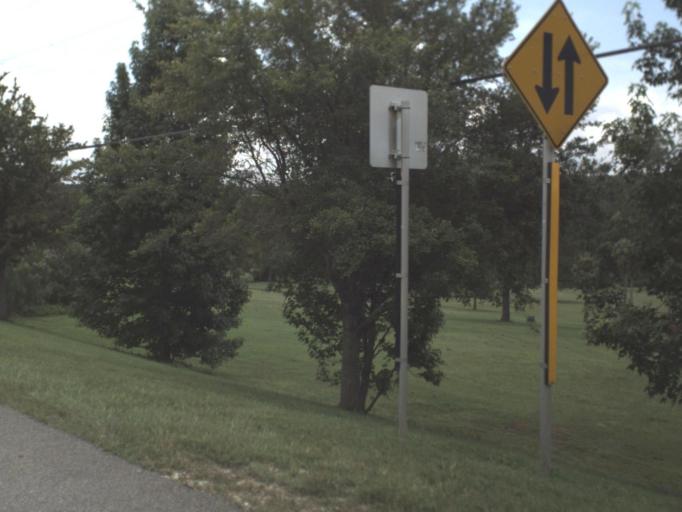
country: US
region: Florida
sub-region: Pasco County
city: Saint Leo
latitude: 28.3356
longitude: -82.2562
